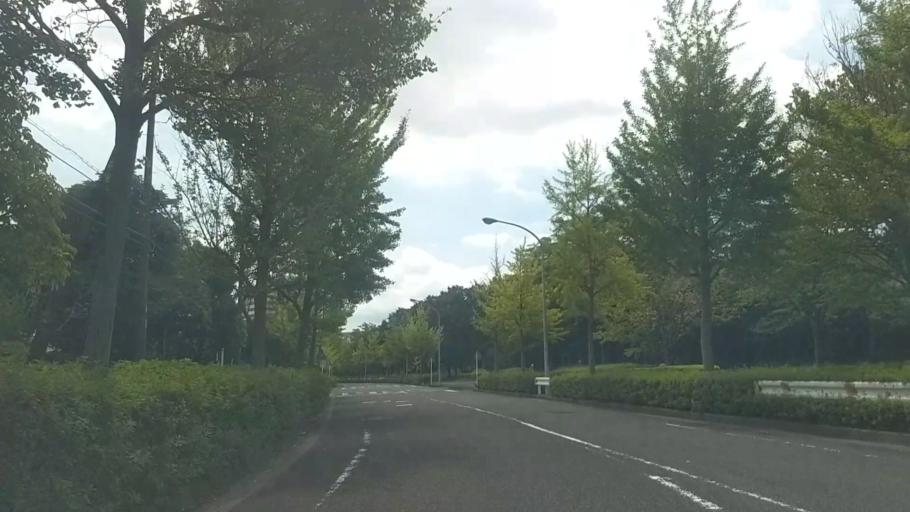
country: JP
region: Kanagawa
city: Yokosuka
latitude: 35.3563
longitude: 139.6390
